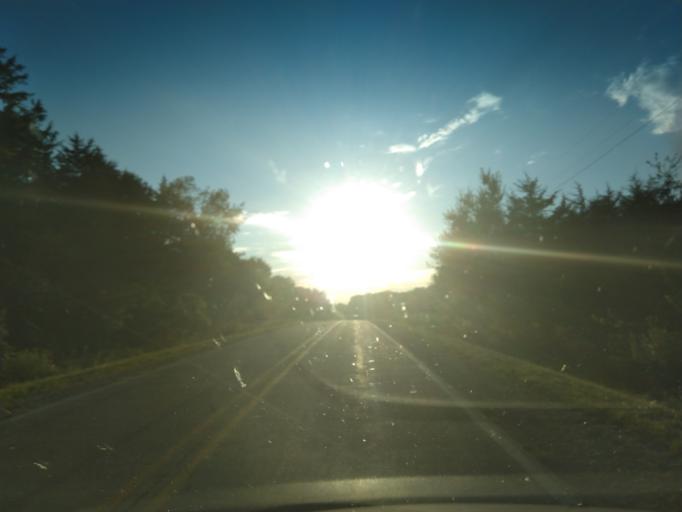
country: US
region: Iowa
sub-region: Jackson County
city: Maquoketa
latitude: 42.1642
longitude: -90.6820
